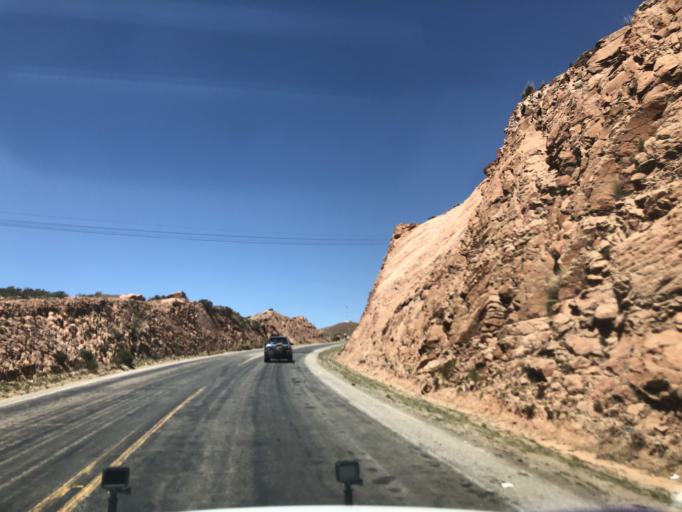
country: BO
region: Cochabamba
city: Colchani
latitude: -17.6894
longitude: -66.7073
